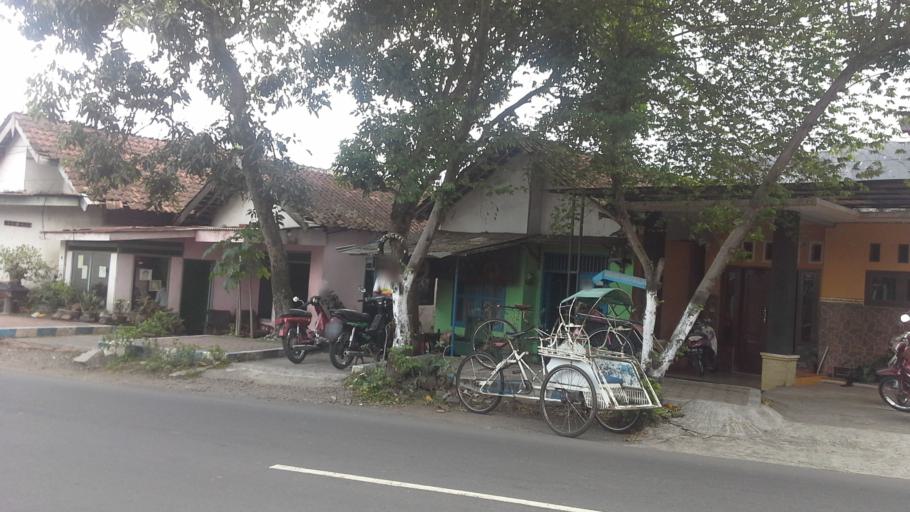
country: ID
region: East Java
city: Bondowoso
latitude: -7.9119
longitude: 113.8464
